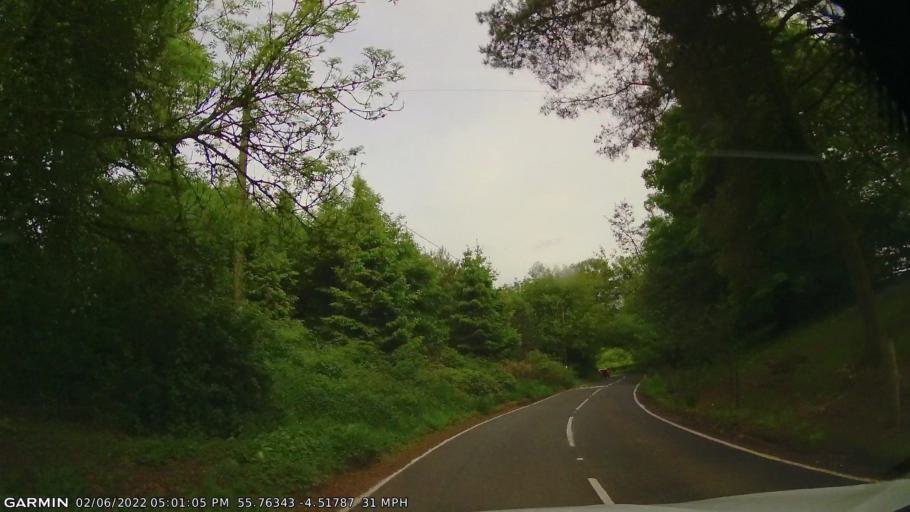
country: GB
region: Scotland
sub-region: Renfrewshire
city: Howwood
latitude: 55.7634
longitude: -4.5179
